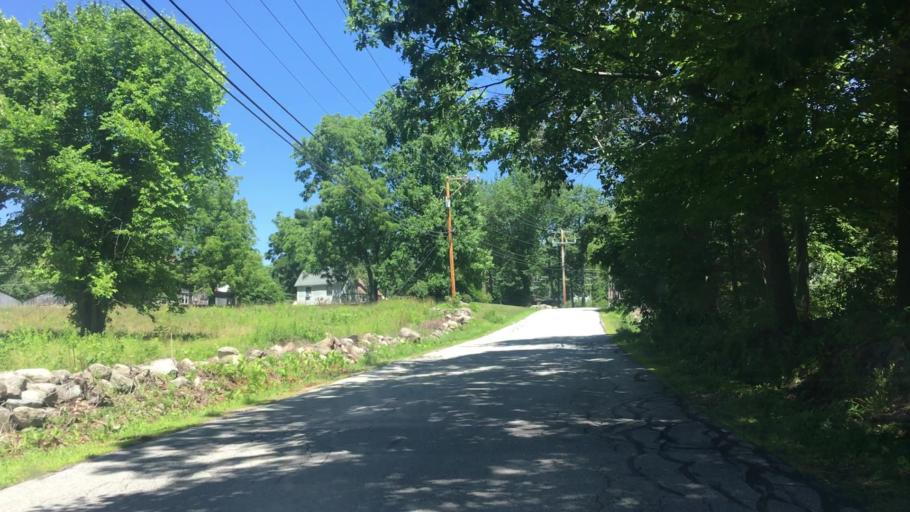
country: US
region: New Hampshire
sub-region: Merrimack County
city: Henniker
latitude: 43.1884
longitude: -71.7861
